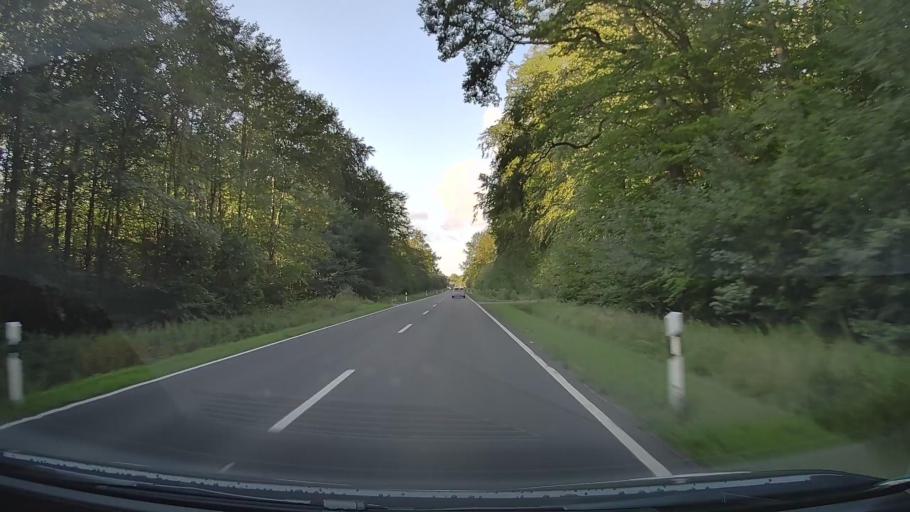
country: DE
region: Mecklenburg-Vorpommern
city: Steinhagen
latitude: 54.2081
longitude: 13.0081
